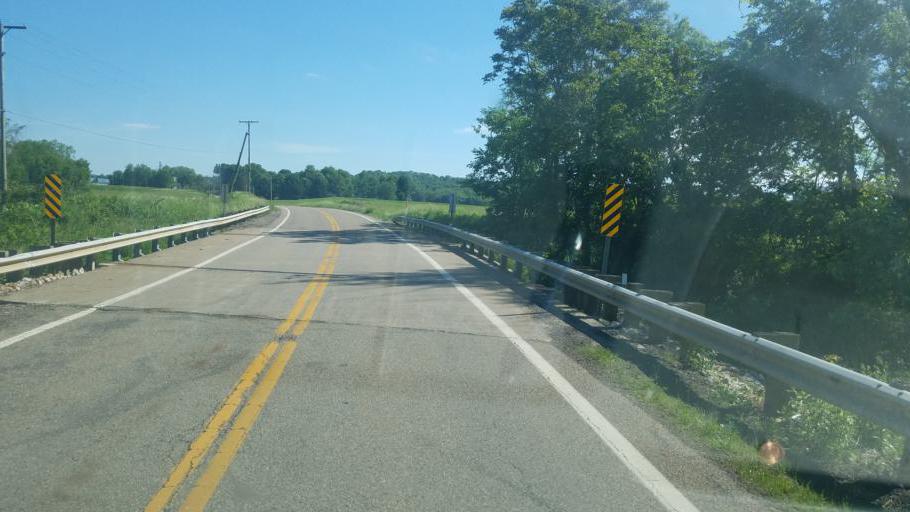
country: US
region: Ohio
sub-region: Coshocton County
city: West Lafayette
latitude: 40.2319
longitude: -81.7317
